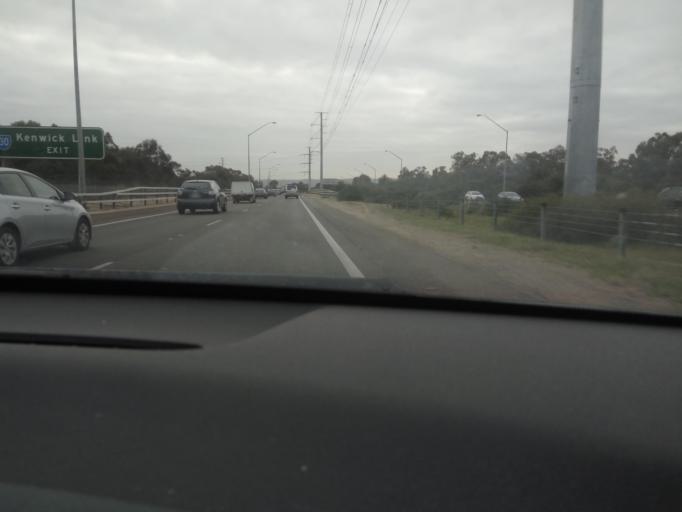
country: AU
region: Western Australia
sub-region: Gosnells
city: Langford
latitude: -32.0409
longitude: 115.9537
